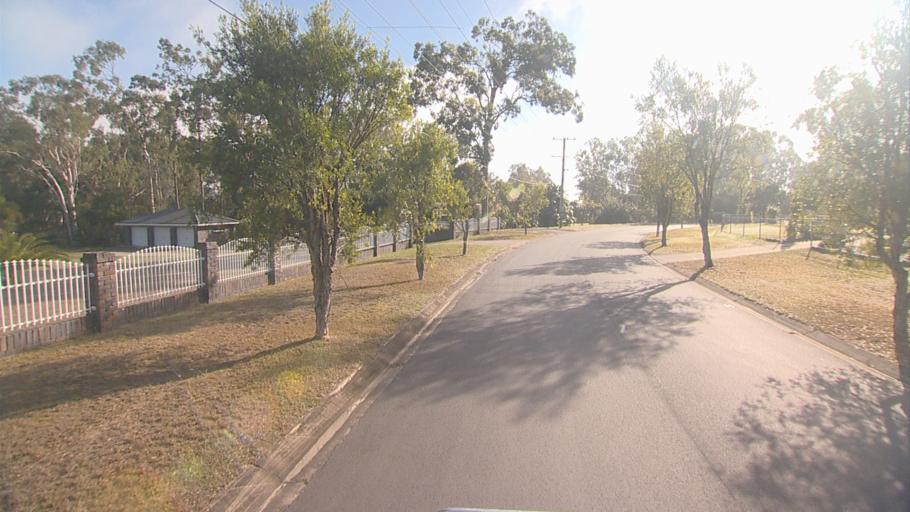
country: AU
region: Queensland
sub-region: Logan
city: Park Ridge South
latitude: -27.6958
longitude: 153.0326
